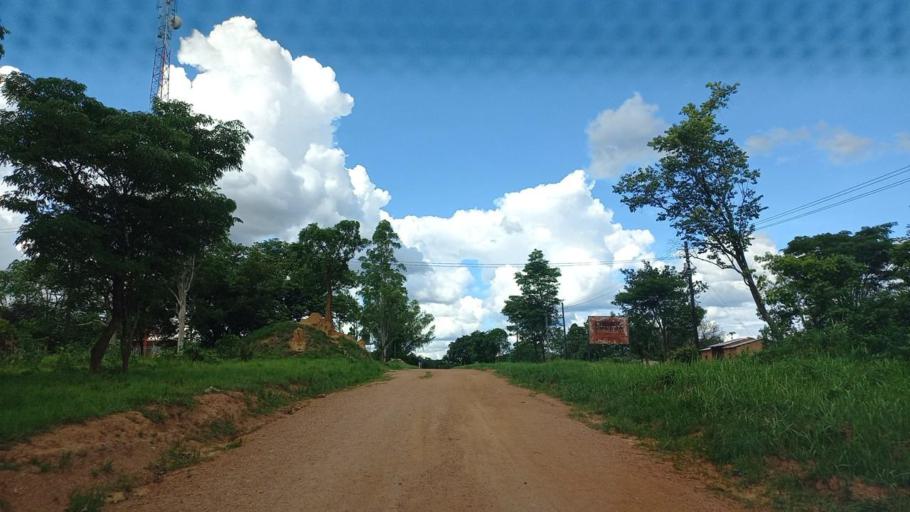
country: ZM
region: North-Western
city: Mwinilunga
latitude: -12.0683
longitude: 24.3015
